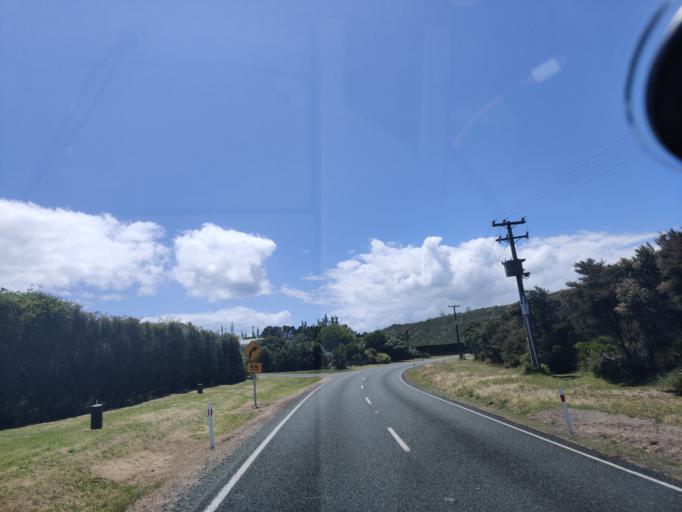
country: NZ
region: Northland
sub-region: Far North District
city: Kaitaia
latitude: -35.0256
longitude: 173.1956
